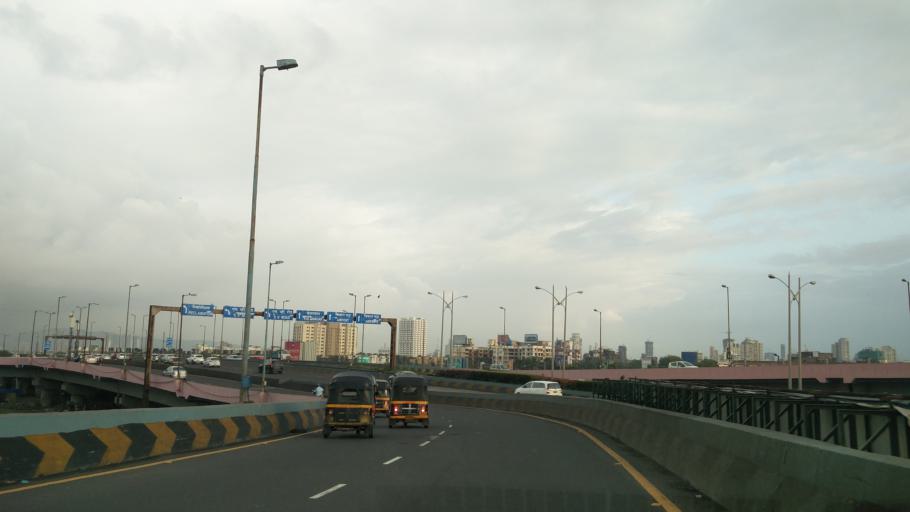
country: IN
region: Maharashtra
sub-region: Mumbai Suburban
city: Mumbai
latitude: 19.0504
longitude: 72.8350
